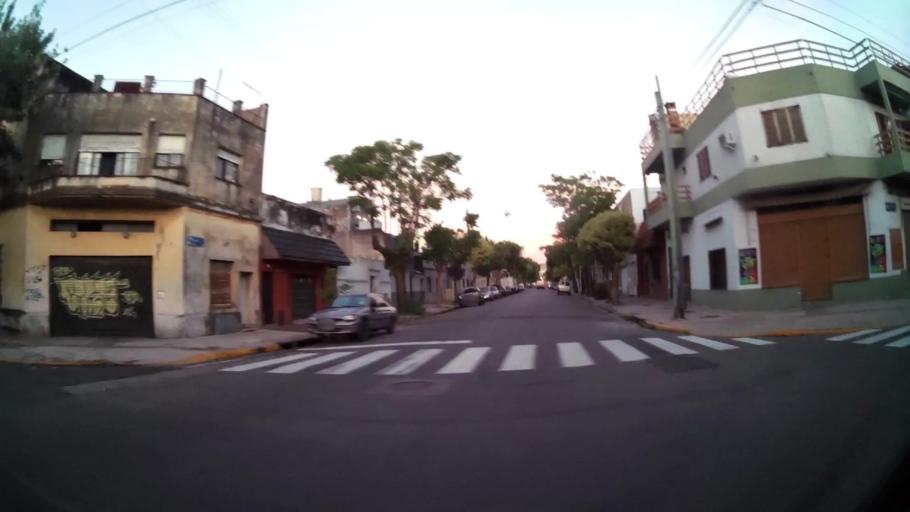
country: AR
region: Buenos Aires F.D.
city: Villa Santa Rita
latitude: -34.6399
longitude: -58.4355
